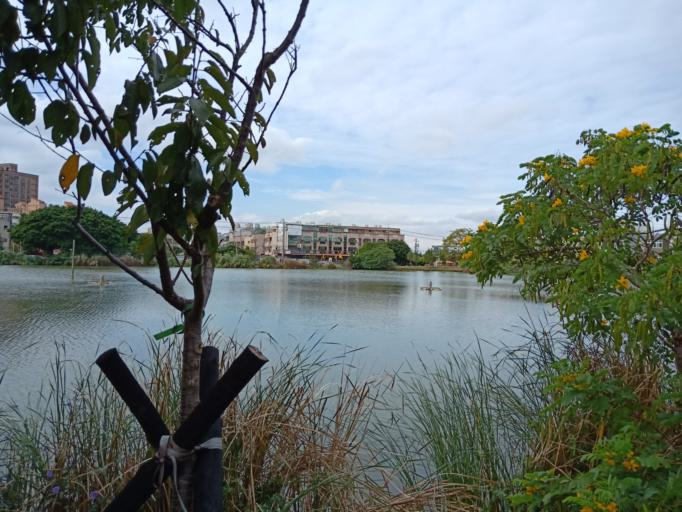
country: TW
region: Taiwan
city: Daxi
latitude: 24.9406
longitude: 121.2582
